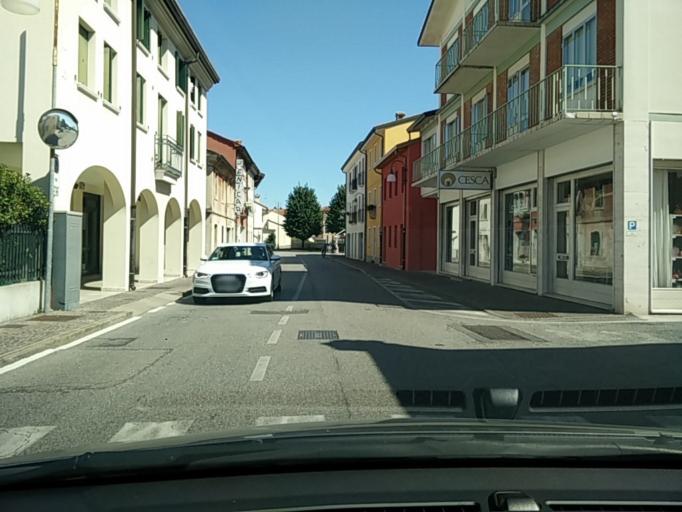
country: IT
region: Veneto
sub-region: Provincia di Venezia
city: Concordia Sagittaria
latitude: 45.7568
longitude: 12.8436
